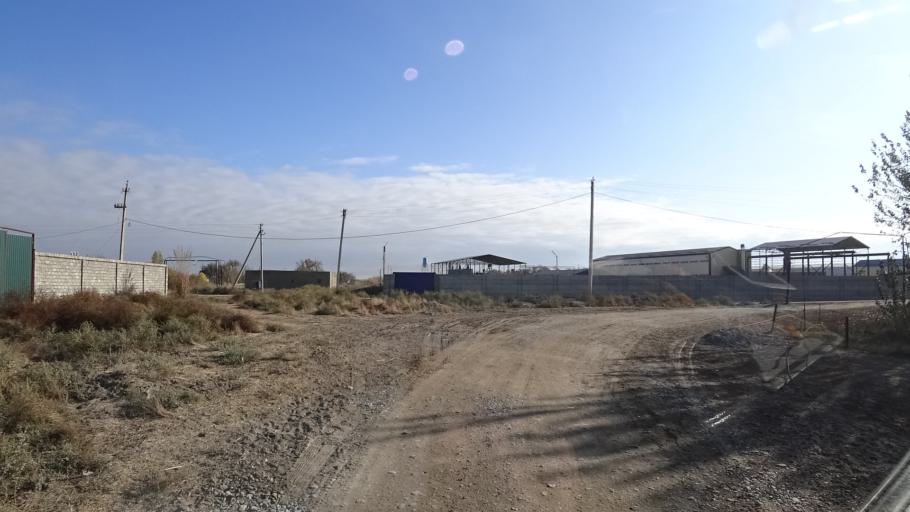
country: UZ
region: Sirdaryo
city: Sirdaryo
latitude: 40.9073
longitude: 68.6811
